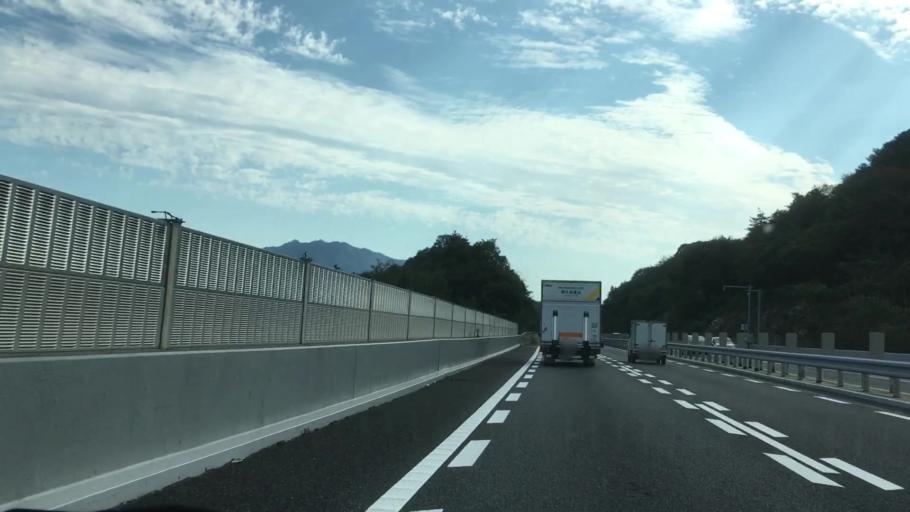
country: JP
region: Hiroshima
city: Ono-hara
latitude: 34.3126
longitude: 132.2806
